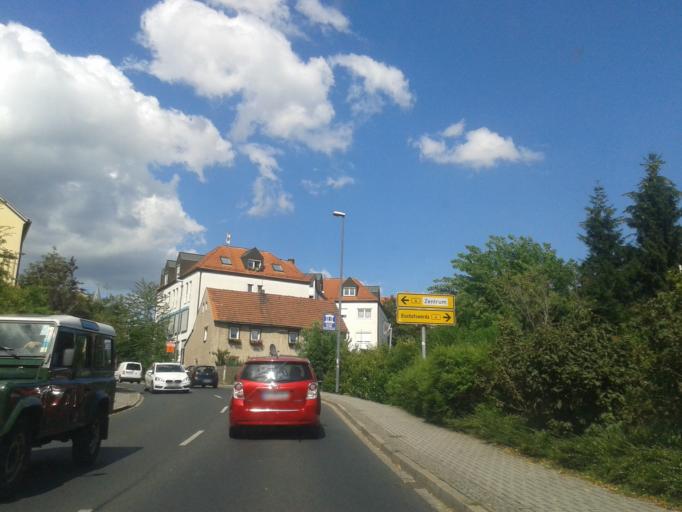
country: DE
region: Saxony
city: Radeberg
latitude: 51.0607
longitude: 13.8473
